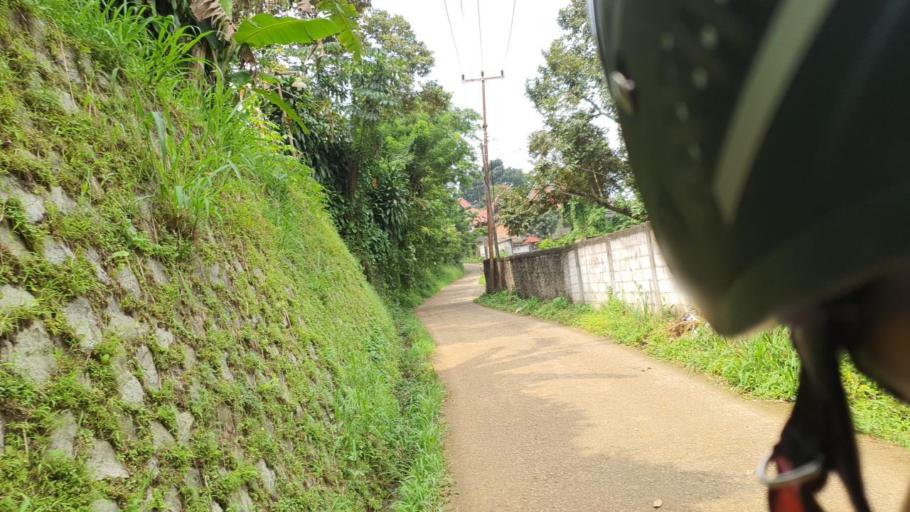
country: ID
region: West Java
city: Caringin
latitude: -6.6524
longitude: 106.8852
